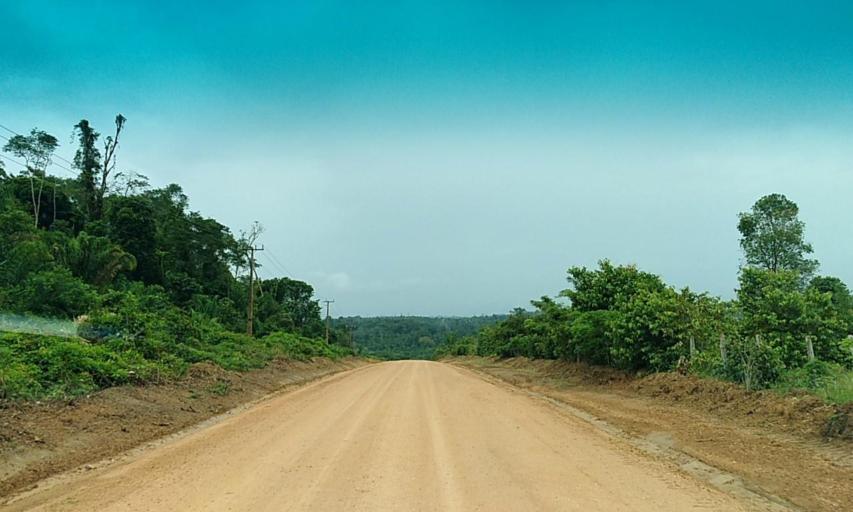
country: BR
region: Para
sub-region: Senador Jose Porfirio
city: Senador Jose Porfirio
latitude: -3.0597
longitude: -51.6545
